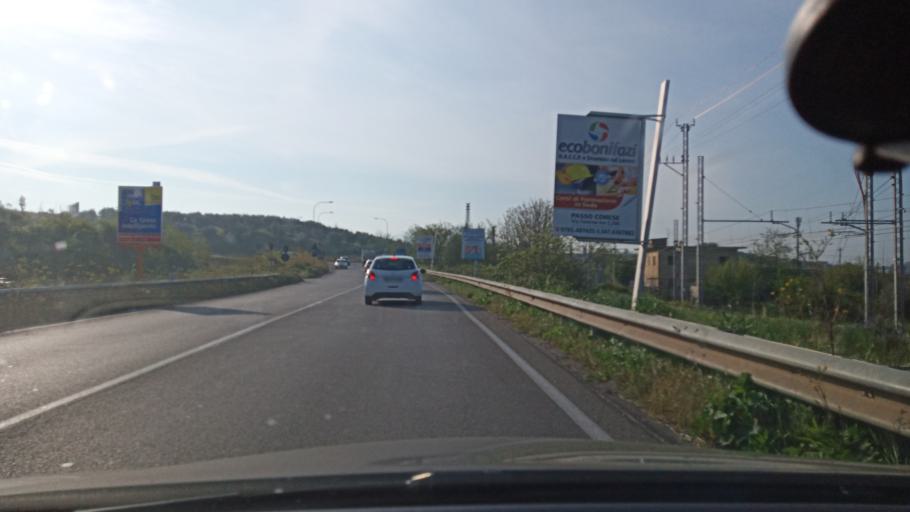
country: IT
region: Latium
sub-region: Citta metropolitana di Roma Capitale
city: Fiano Romano
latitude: 42.1637
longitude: 12.6453
